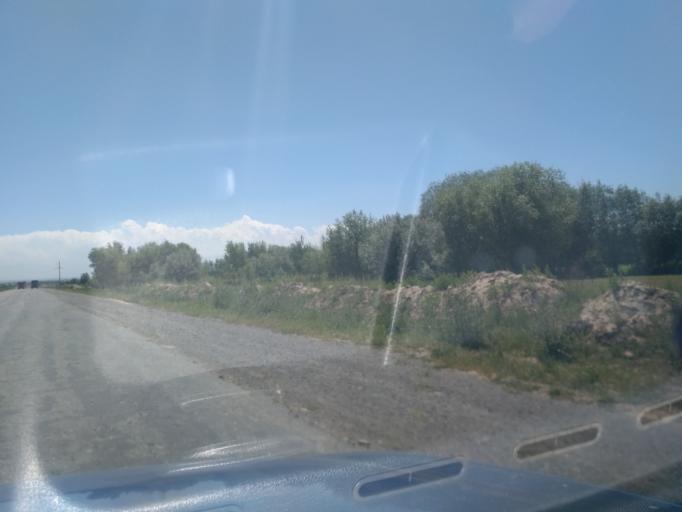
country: UZ
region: Sirdaryo
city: Yangiyer
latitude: 40.2307
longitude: 68.8480
